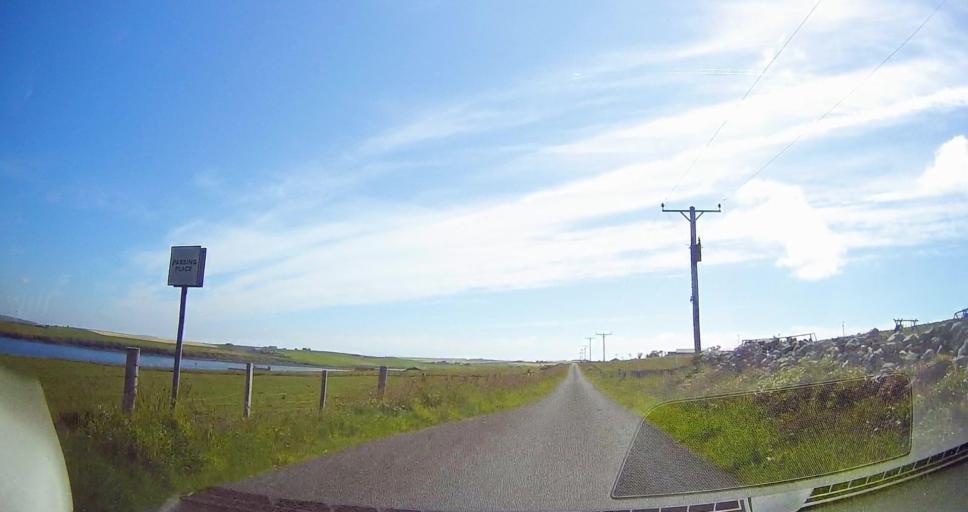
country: GB
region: Scotland
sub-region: Orkney Islands
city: Kirkwall
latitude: 58.8571
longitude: -2.9355
